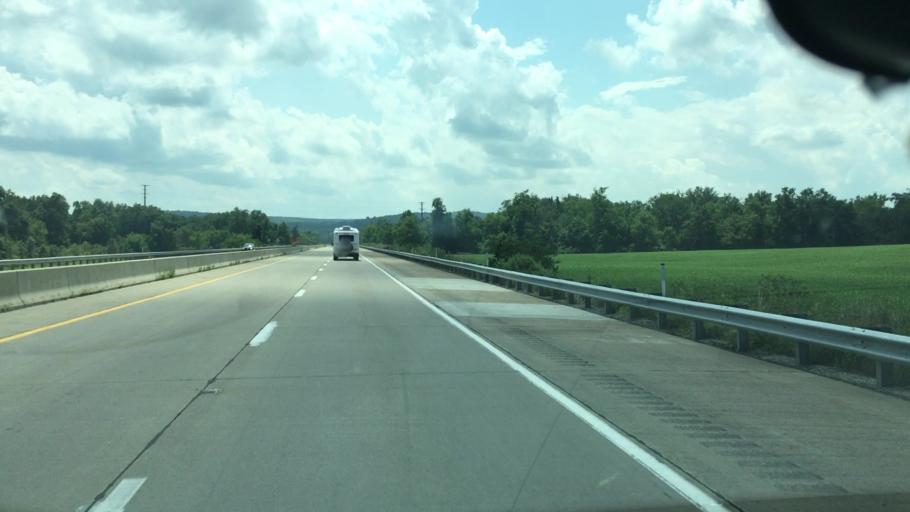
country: US
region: Pennsylvania
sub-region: Dauphin County
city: Millersburg
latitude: 40.6448
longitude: -76.9361
